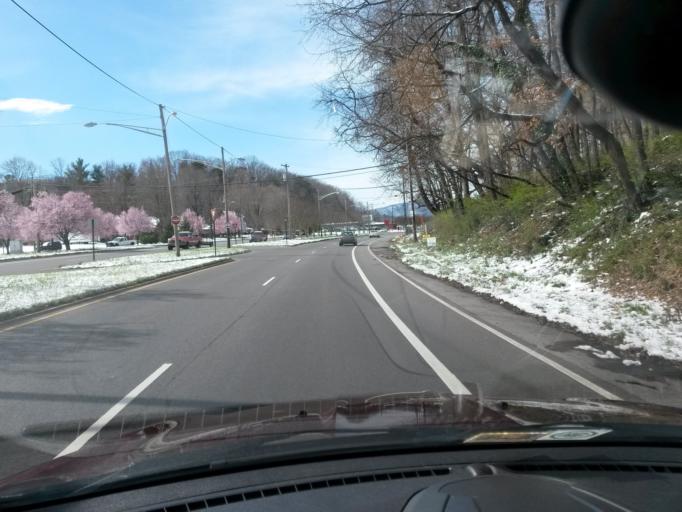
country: US
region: Virginia
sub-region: Roanoke County
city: Narrows
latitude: 37.2394
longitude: -79.9660
